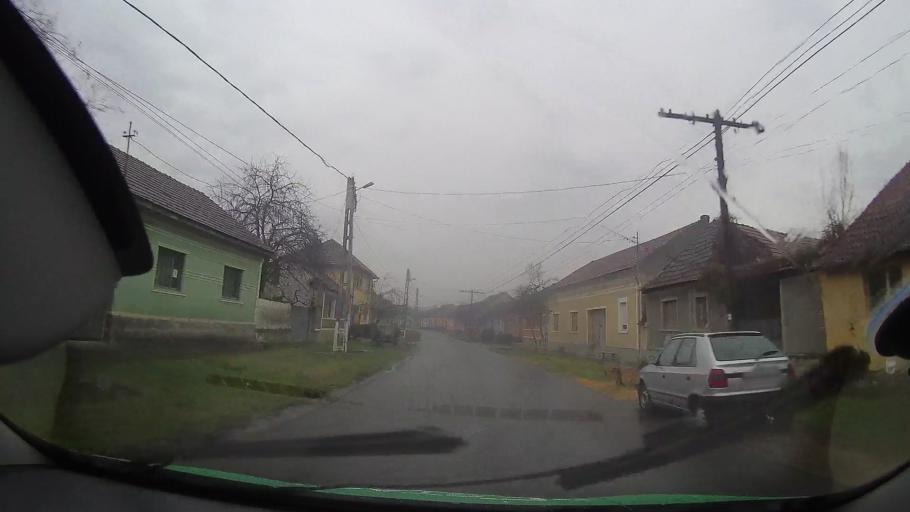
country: RO
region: Bihor
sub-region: Comuna Uileacu de Beius
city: Uileacu de Beius
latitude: 46.6820
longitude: 22.2242
